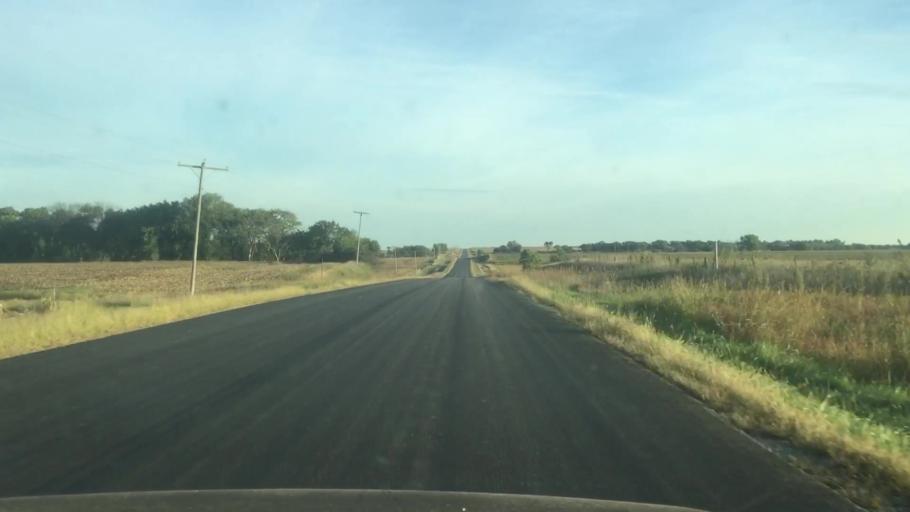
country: US
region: Kansas
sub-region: Marshall County
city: Marysville
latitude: 39.8742
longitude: -96.6009
